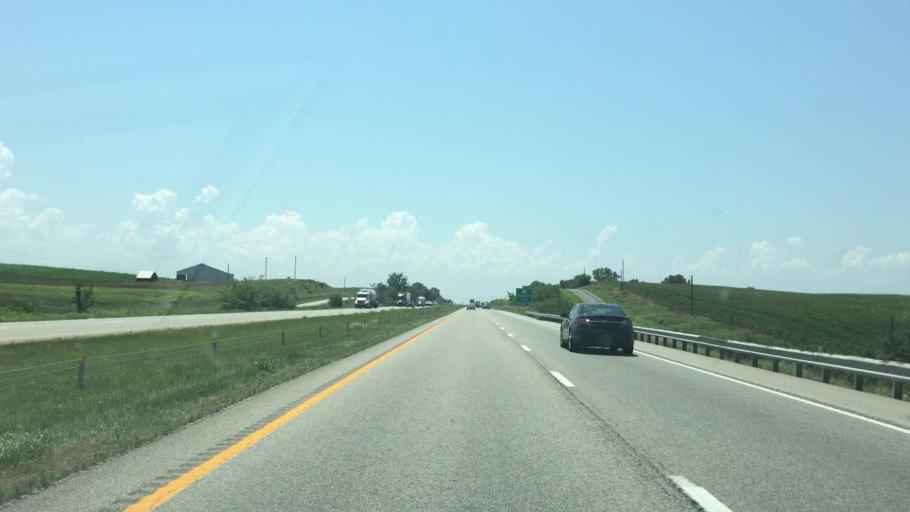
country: US
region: Kansas
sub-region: Doniphan County
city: Elwood
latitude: 39.6179
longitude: -94.7884
